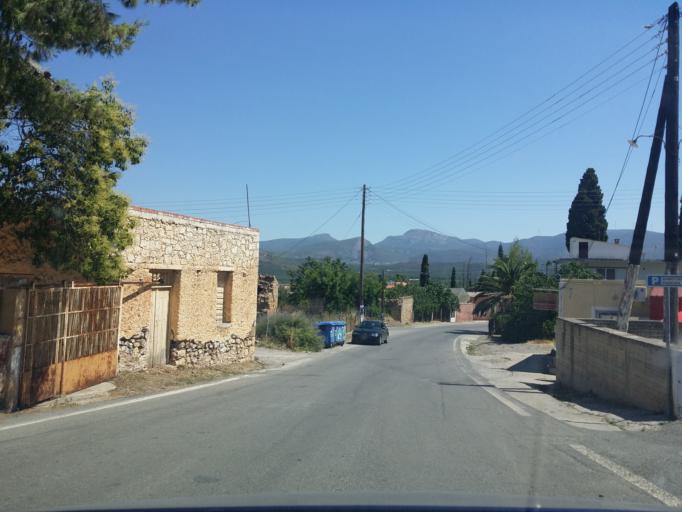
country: GR
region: Peloponnese
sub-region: Nomos Lakonias
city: Kato Glikovrisi
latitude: 36.8823
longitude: 22.7982
